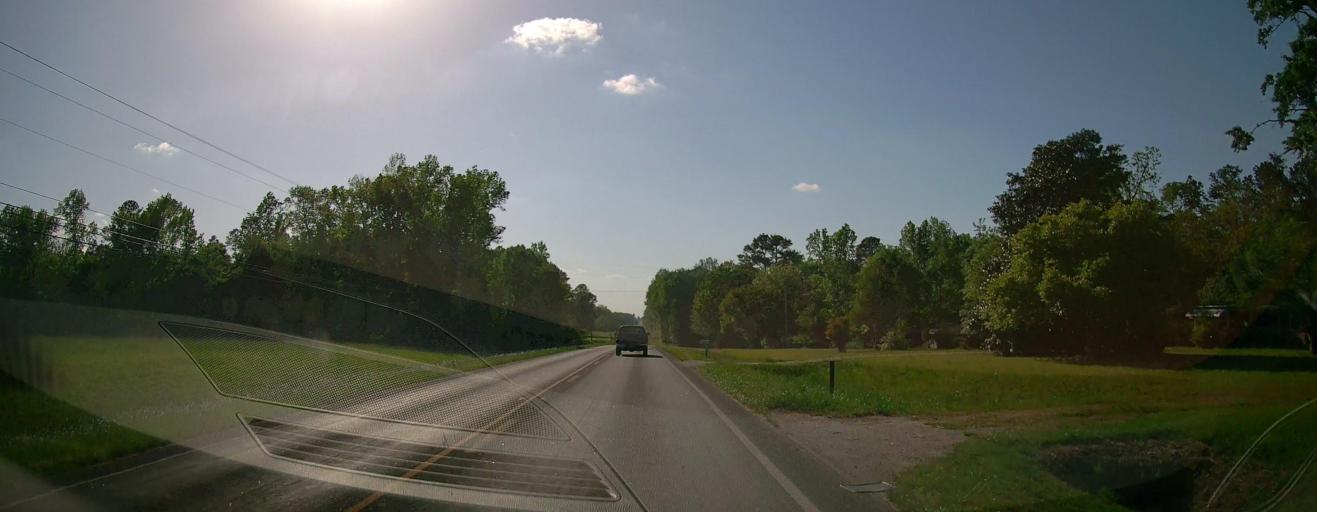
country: US
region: Georgia
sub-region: Morgan County
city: Madison
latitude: 33.5819
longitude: -83.4929
